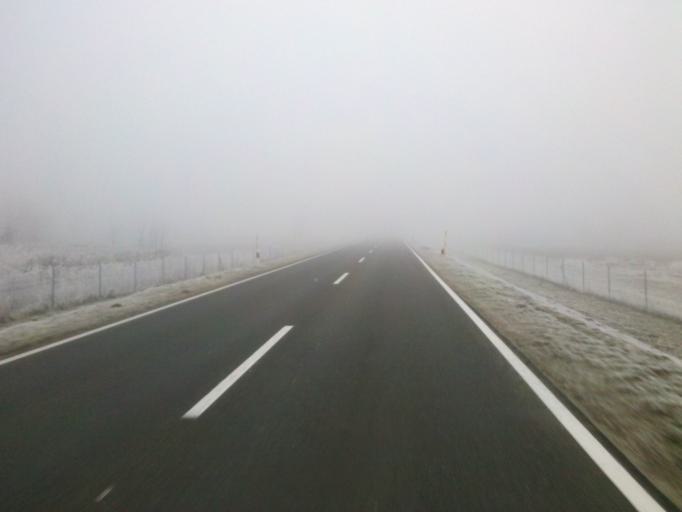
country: HR
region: Varazdinska
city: Jalkovec
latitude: 46.2787
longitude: 16.3064
